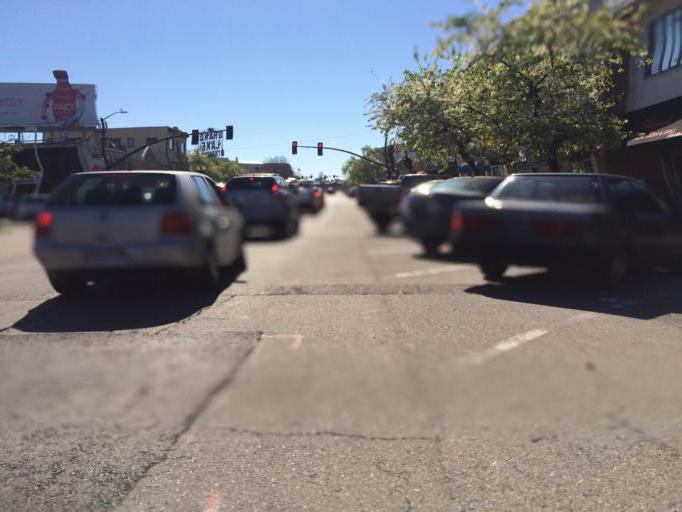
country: US
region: California
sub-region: Alameda County
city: Piedmont
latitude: 37.8143
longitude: -122.2463
